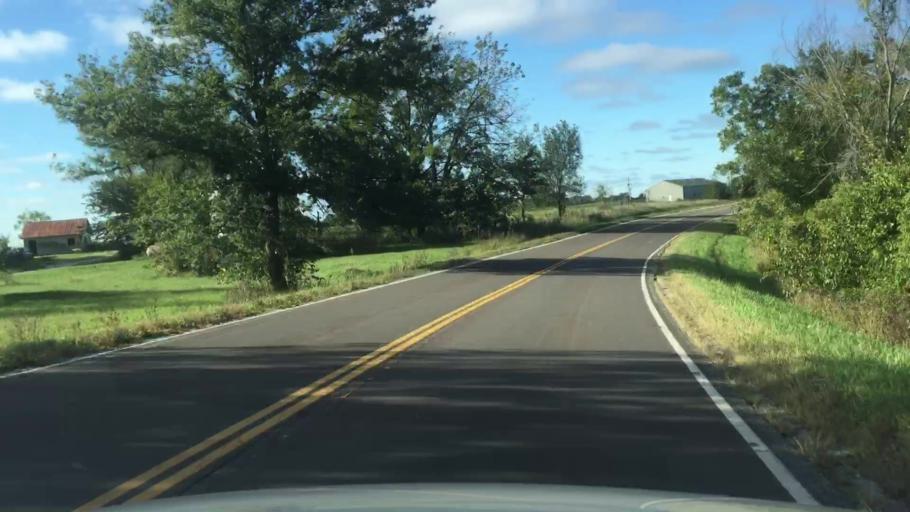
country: US
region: Missouri
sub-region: Howard County
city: Fayette
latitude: 39.0997
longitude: -92.7368
